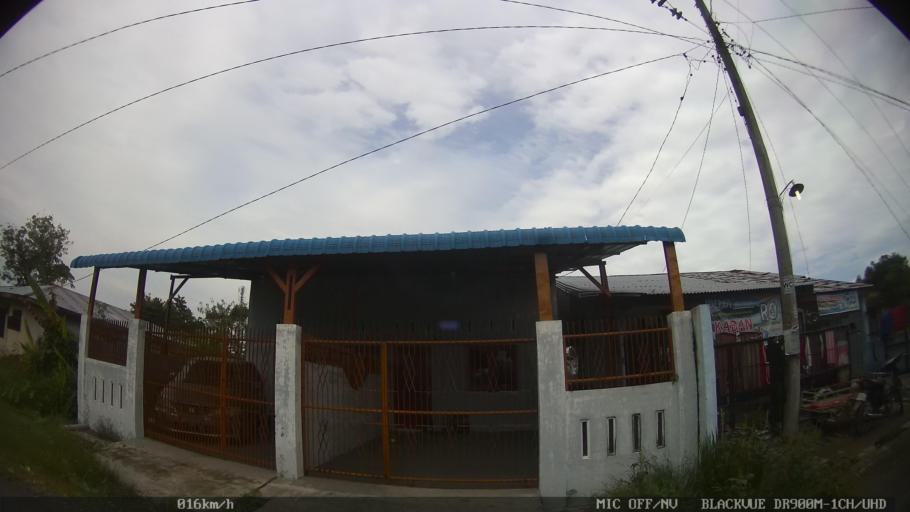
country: ID
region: North Sumatra
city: Sunggal
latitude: 3.6197
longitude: 98.5936
